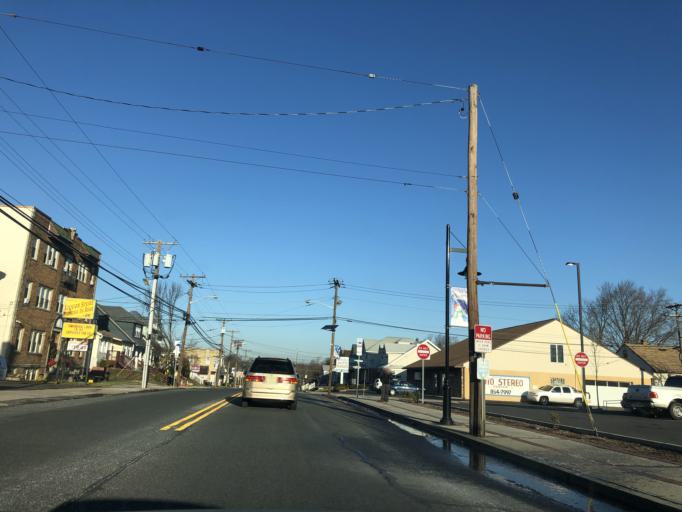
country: US
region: New Jersey
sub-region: Camden County
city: Oaklyn
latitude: 39.9055
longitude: -75.0797
